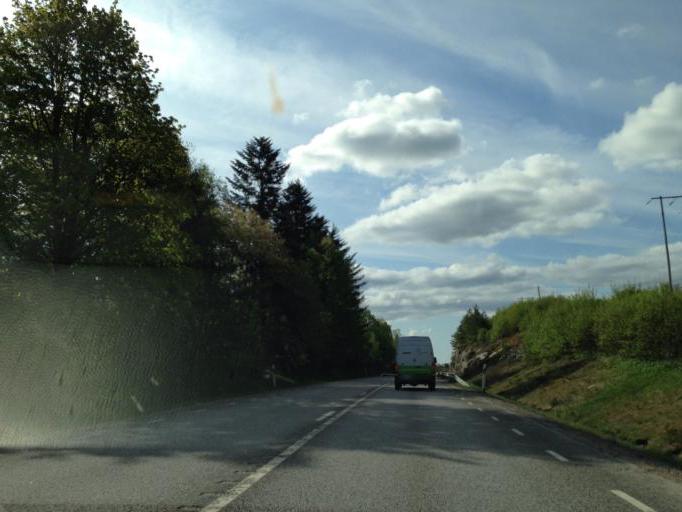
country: SE
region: Soedermanland
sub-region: Nykopings Kommun
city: Nykoping
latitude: 58.8271
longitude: 16.9286
